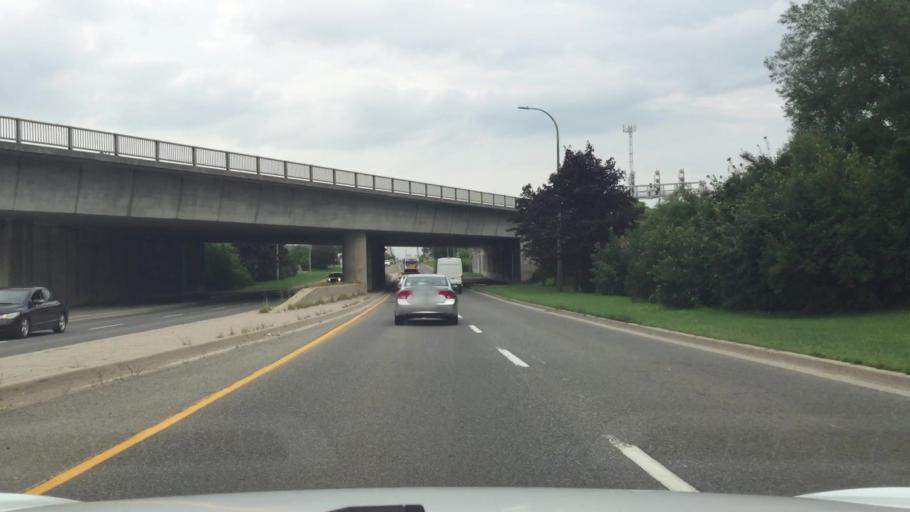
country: CA
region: Ontario
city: Oshawa
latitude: 43.8632
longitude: -78.9307
